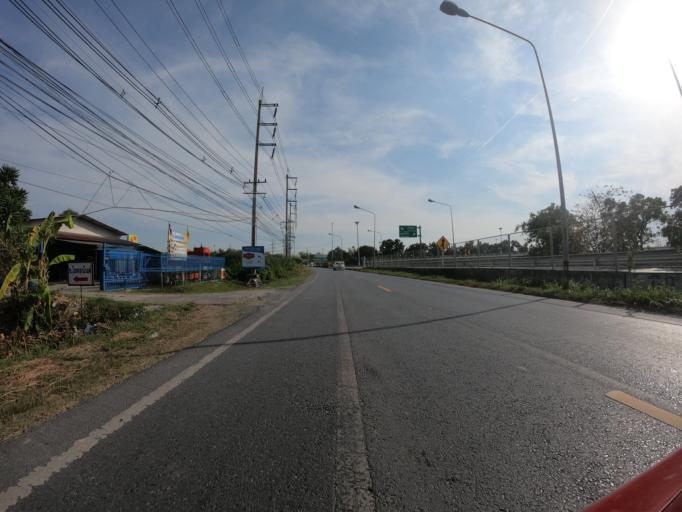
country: TH
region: Pathum Thani
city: Lam Luk Ka
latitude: 13.9362
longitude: 100.7101
